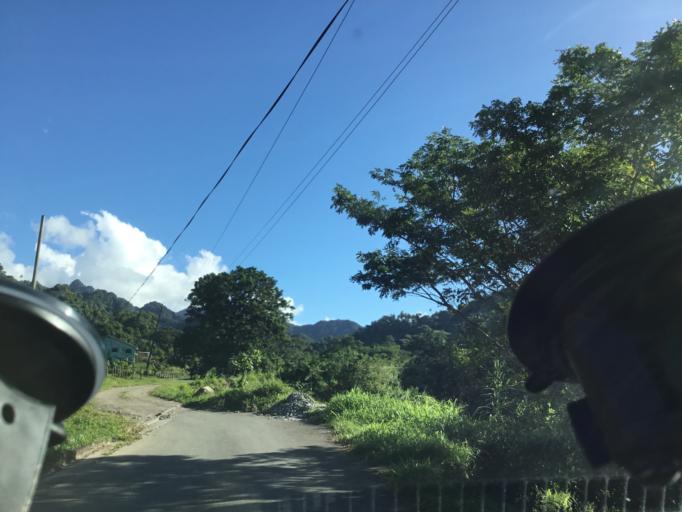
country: VC
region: Saint David
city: Chateaubelair
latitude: 13.3058
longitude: -61.2297
